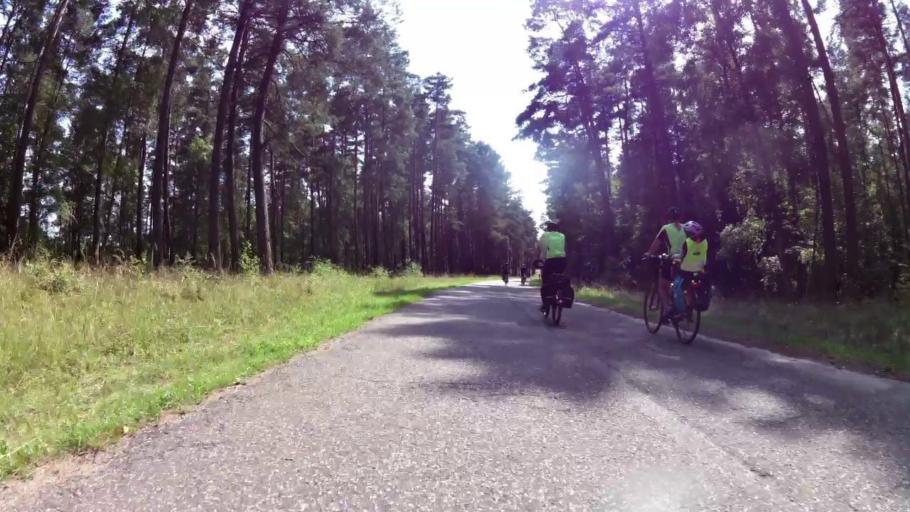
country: PL
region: West Pomeranian Voivodeship
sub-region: Powiat choszczenski
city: Drawno
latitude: 53.3308
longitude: 15.6958
